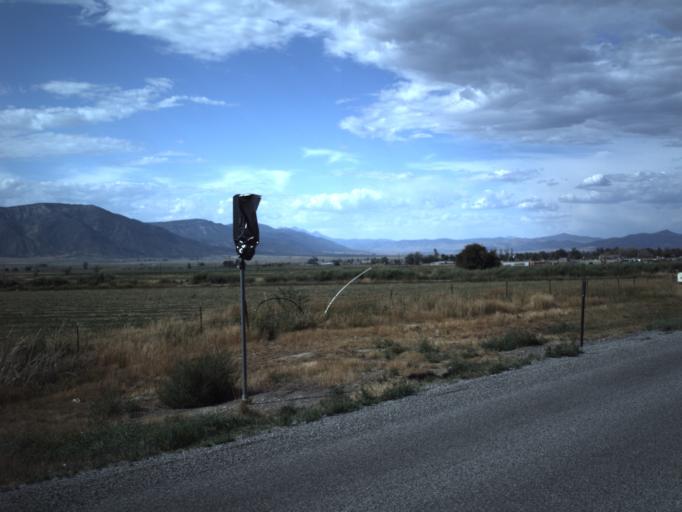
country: US
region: Utah
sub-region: Sanpete County
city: Ephraim
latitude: 39.3399
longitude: -111.5944
